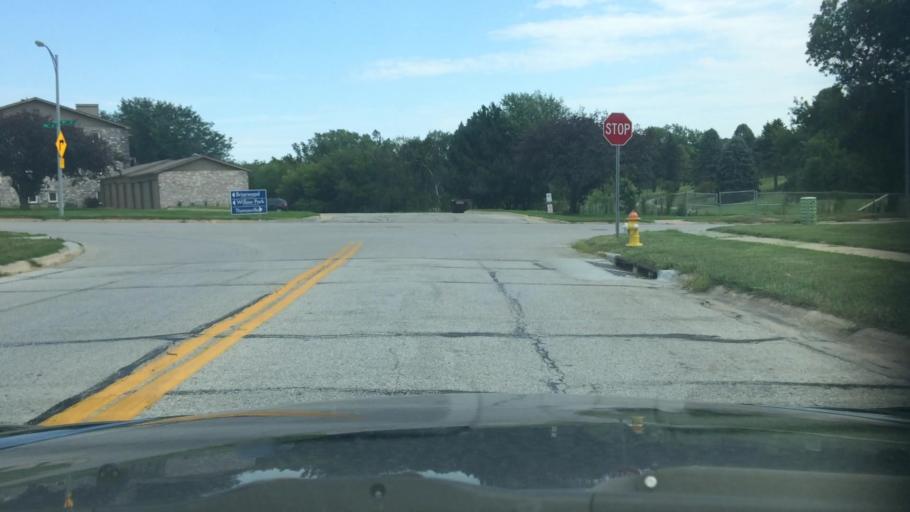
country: US
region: Nebraska
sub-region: Douglas County
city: Ralston
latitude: 41.2026
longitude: -96.0669
